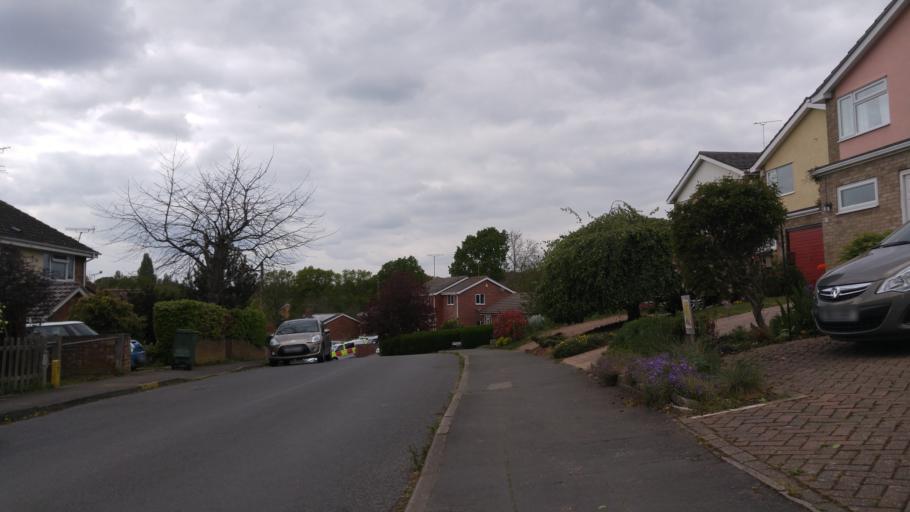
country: GB
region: England
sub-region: Essex
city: Earls Colne
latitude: 51.9412
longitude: 0.6881
